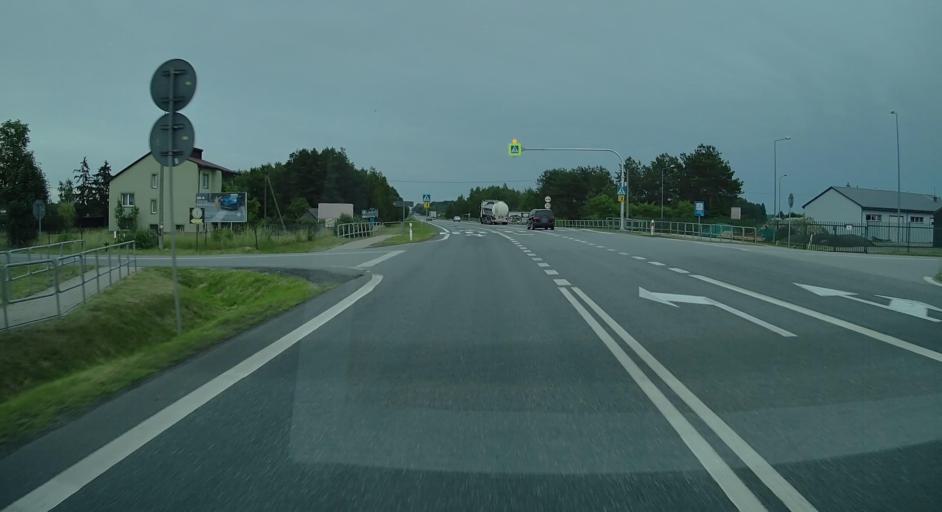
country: PL
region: Lublin Voivodeship
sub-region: Powiat bialski
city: Rokitno
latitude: 52.0341
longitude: 23.2703
